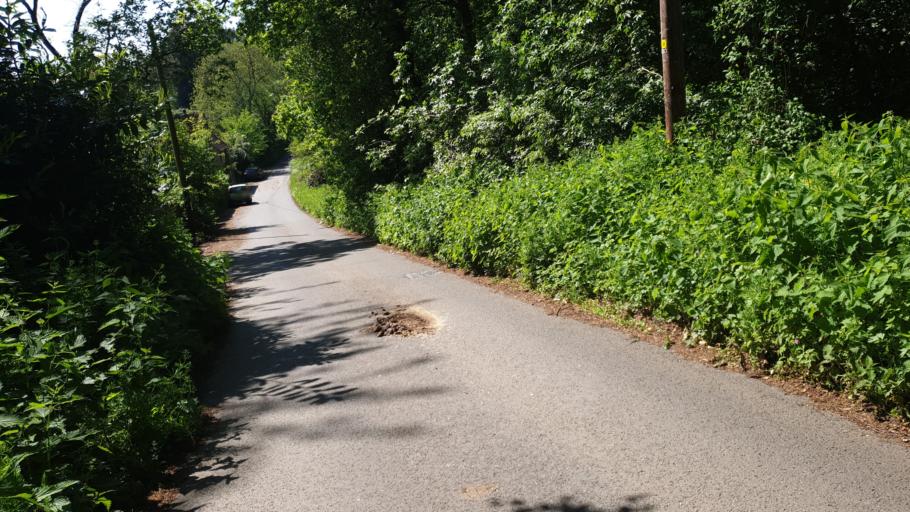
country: GB
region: England
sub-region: Essex
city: Manningtree
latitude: 51.9420
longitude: 1.0376
